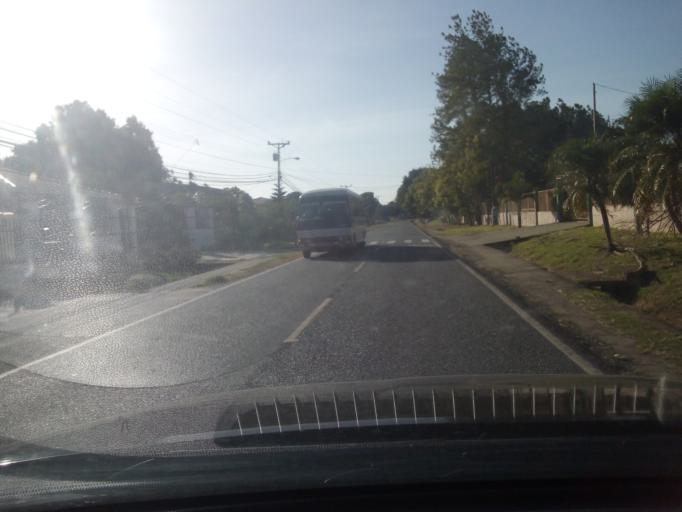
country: PA
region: Veraguas
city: Atalaya
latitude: 8.0456
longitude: -80.9287
